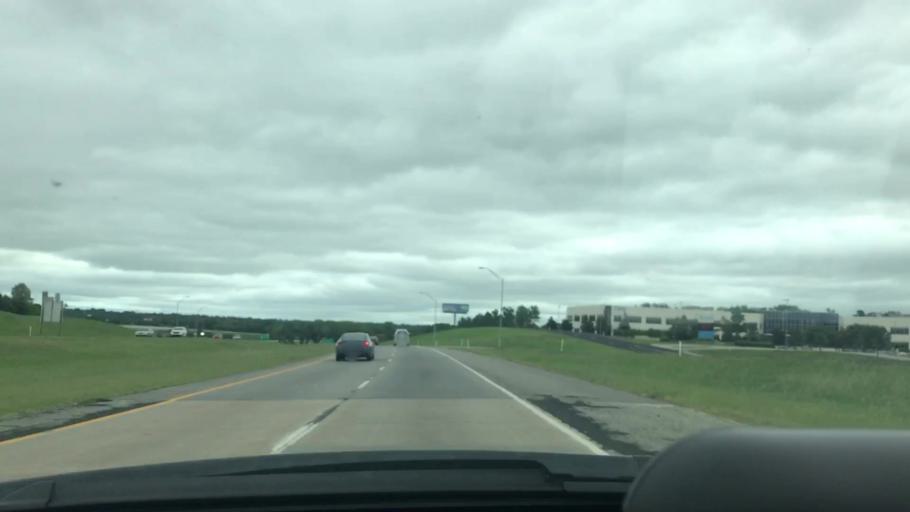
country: US
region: Texas
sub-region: Grayson County
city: Denison
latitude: 33.7112
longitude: -96.5875
